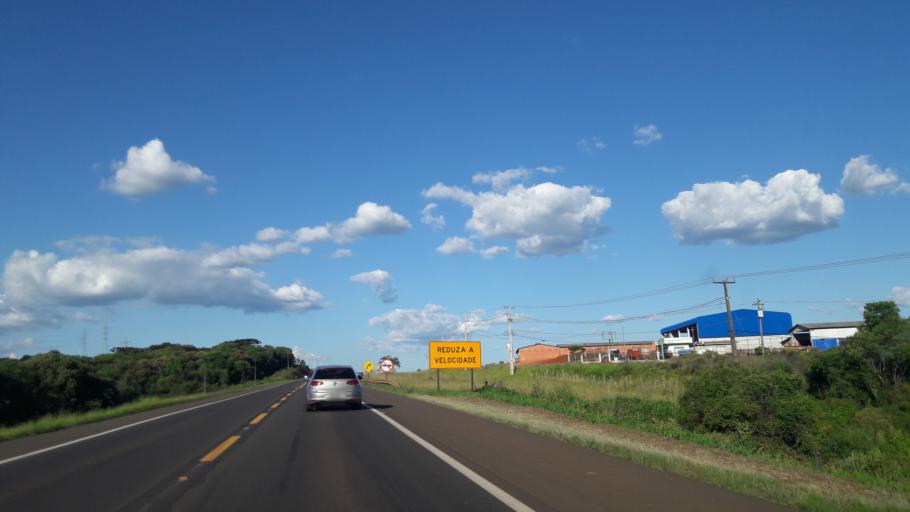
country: BR
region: Parana
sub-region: Guarapuava
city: Guarapuava
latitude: -25.3733
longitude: -51.5011
